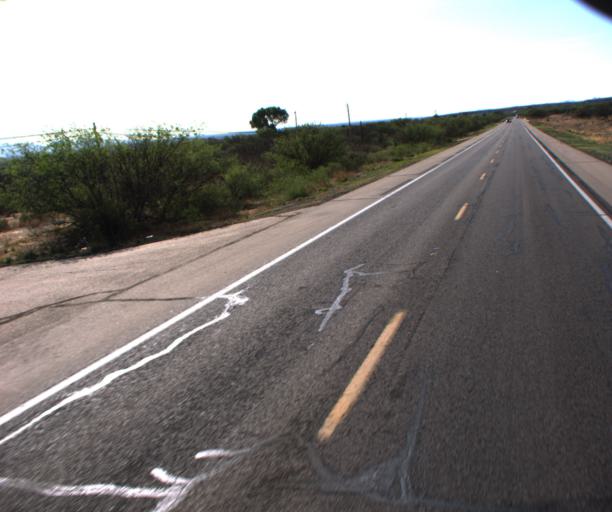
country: US
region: Arizona
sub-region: Cochise County
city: Saint David
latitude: 31.9165
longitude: -110.2634
